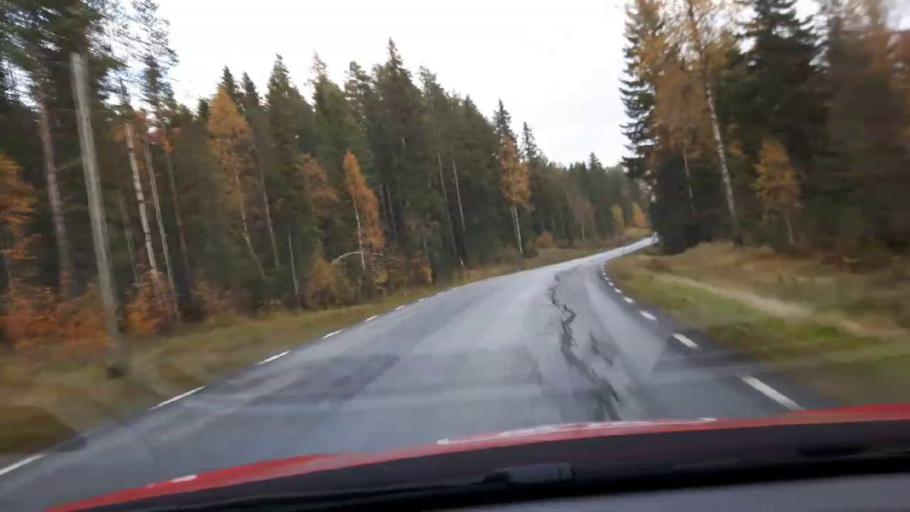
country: SE
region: Jaemtland
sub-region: OEstersunds Kommun
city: Lit
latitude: 63.3227
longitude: 14.9385
